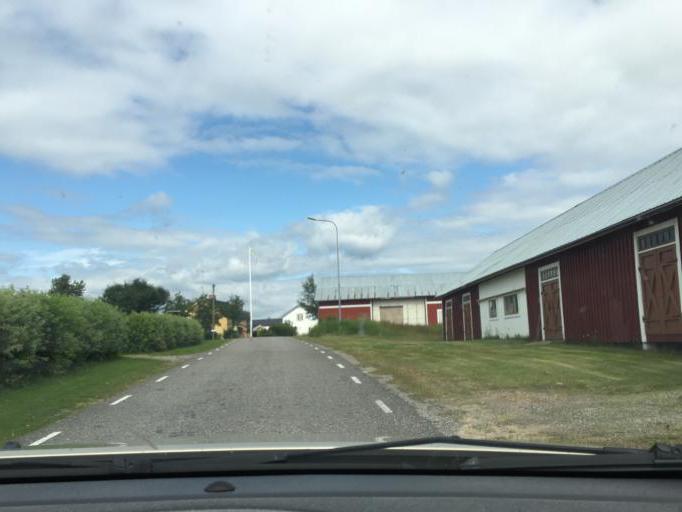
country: SE
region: Norrbotten
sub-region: Overkalix Kommun
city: OEverkalix
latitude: 66.1058
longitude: 22.7826
